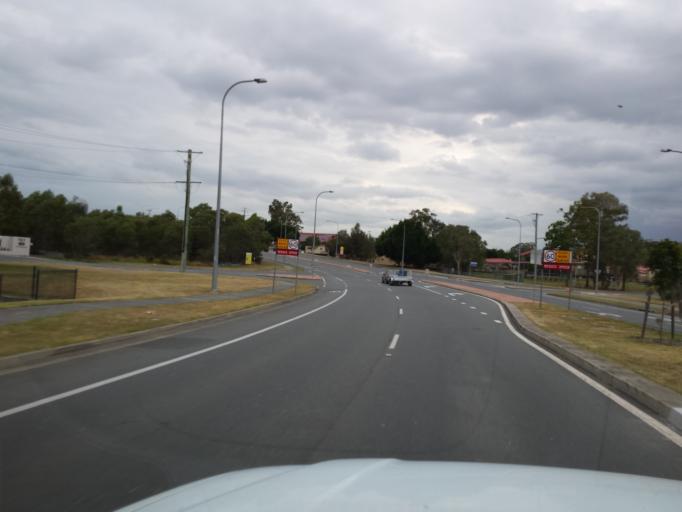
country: AU
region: Queensland
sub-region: Gold Coast
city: Oxenford
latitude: -27.8556
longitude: 153.3034
